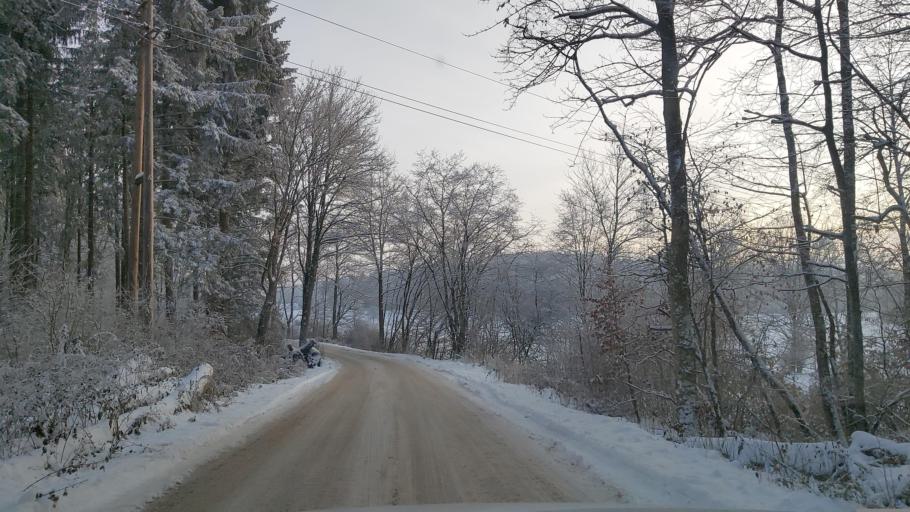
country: DE
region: Baden-Wuerttemberg
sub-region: Tuebingen Region
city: Eningen unter Achalm
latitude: 48.4922
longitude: 9.3028
